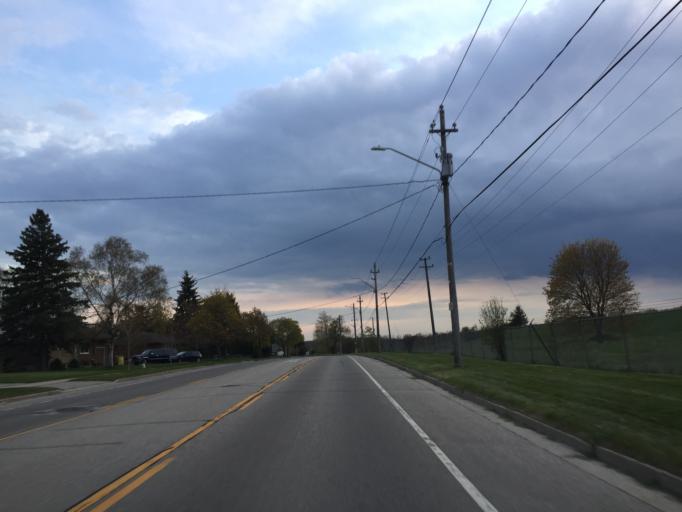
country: CA
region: Ontario
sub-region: Wellington County
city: Guelph
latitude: 43.5164
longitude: -80.2542
